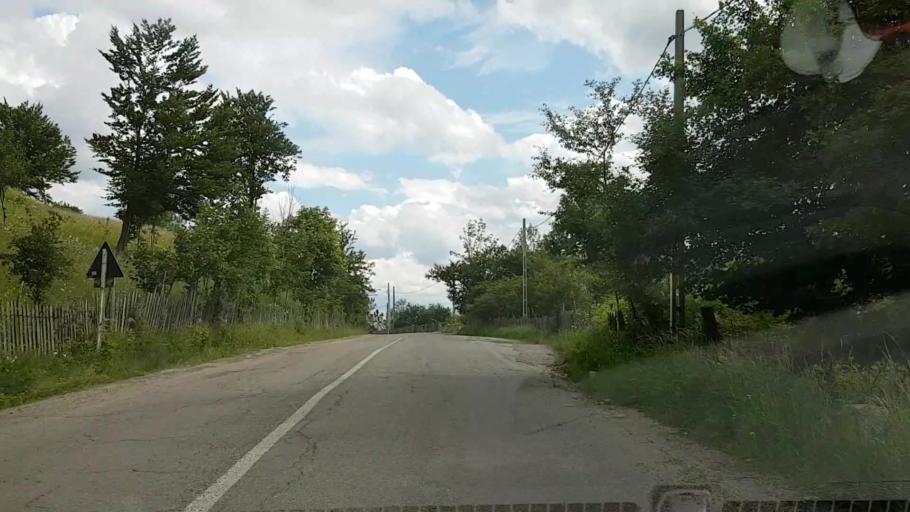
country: RO
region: Neamt
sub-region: Comuna Bicaz
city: Dodeni
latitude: 46.9884
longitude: 26.1019
